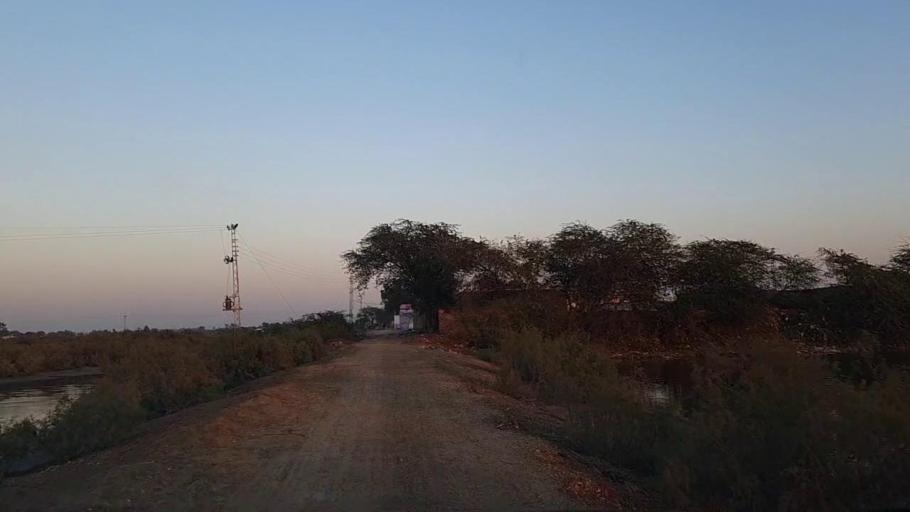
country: PK
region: Sindh
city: Nawabshah
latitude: 26.2932
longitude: 68.4293
